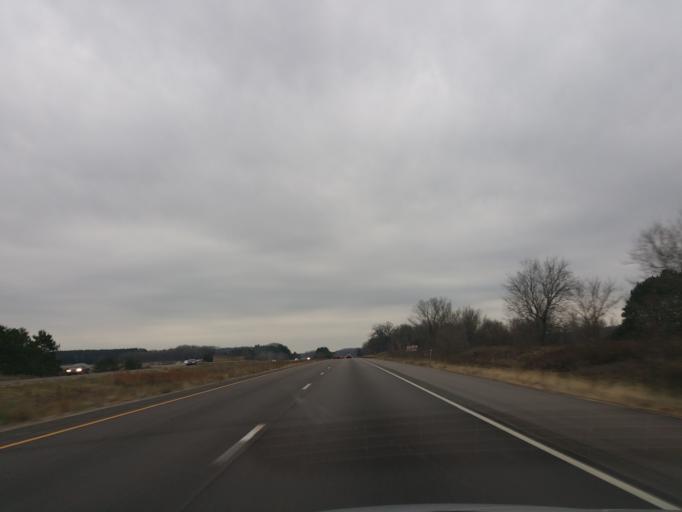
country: US
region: Wisconsin
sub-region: Eau Claire County
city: Fall Creek
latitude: 44.7122
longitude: -91.3468
